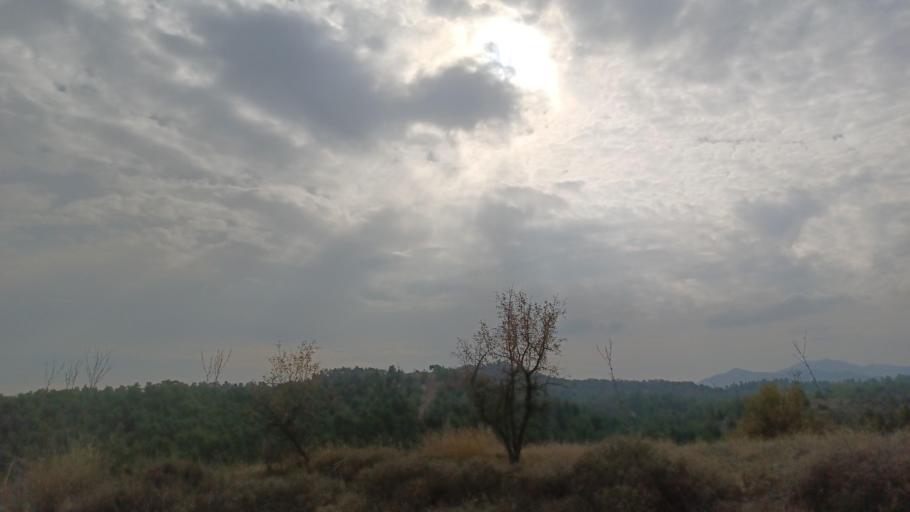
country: CY
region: Lefkosia
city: Klirou
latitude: 35.0405
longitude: 33.1098
